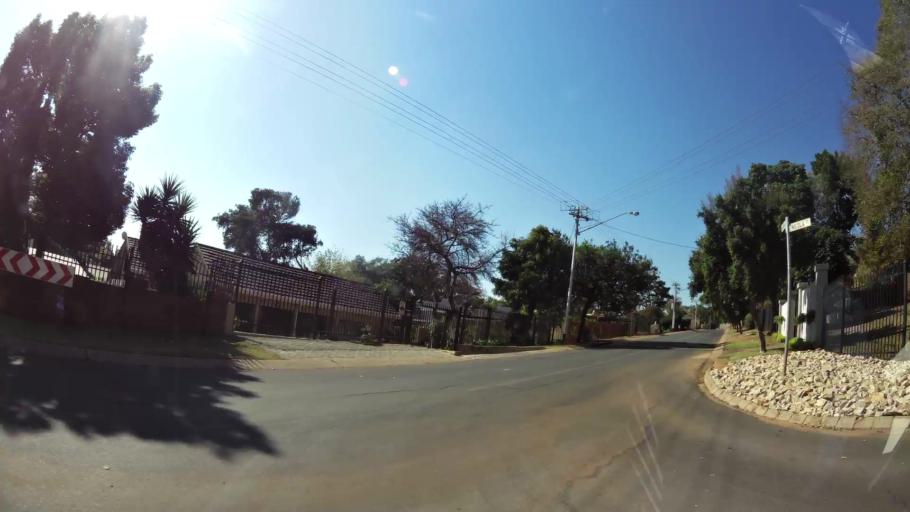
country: ZA
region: Gauteng
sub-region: City of Tshwane Metropolitan Municipality
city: Pretoria
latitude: -25.6883
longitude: 28.2184
